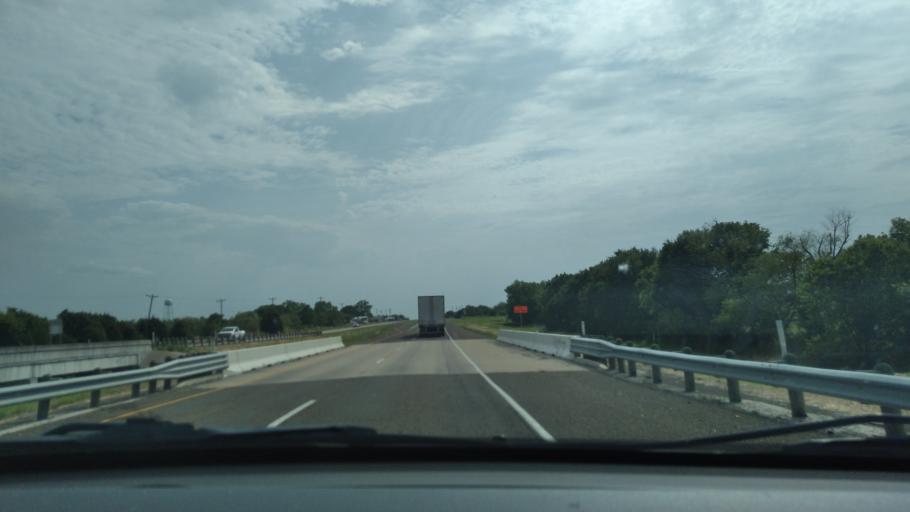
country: US
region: Texas
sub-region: Navarro County
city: Corsicana
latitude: 32.0403
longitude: -96.5439
